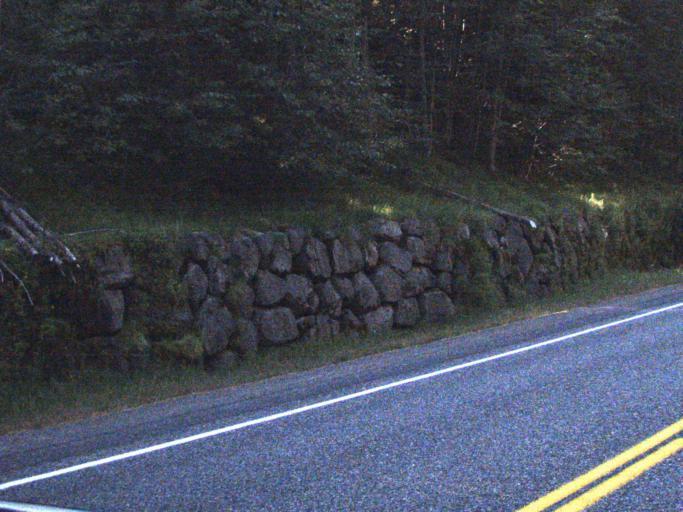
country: US
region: Washington
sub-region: King County
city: Enumclaw
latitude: 47.0018
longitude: -121.5287
